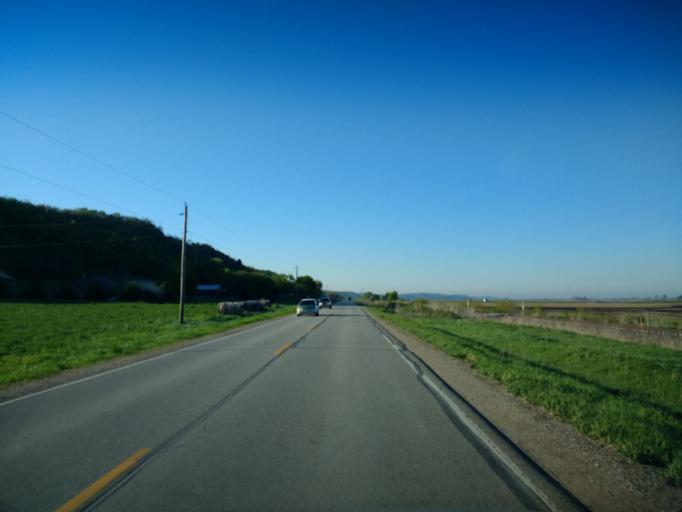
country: US
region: Iowa
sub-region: Harrison County
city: Missouri Valley
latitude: 41.4801
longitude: -95.8838
